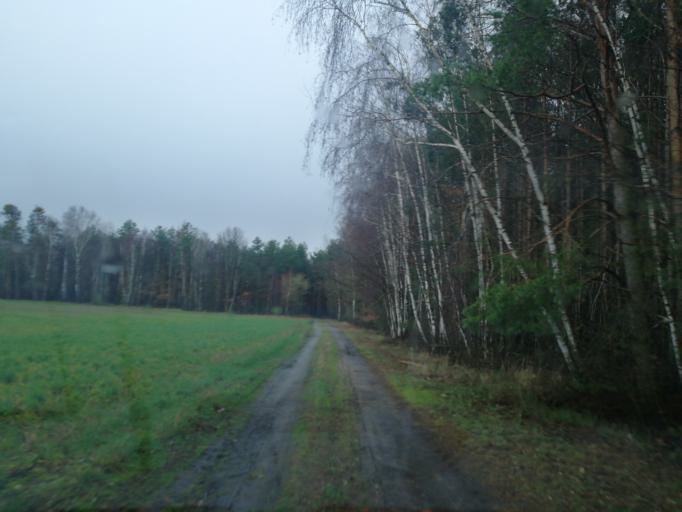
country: DE
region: Brandenburg
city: Schonborn
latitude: 51.6687
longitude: 13.4890
